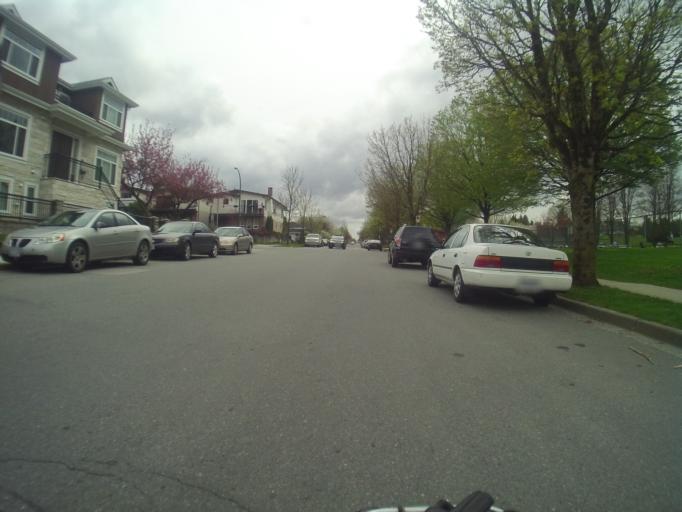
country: CA
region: British Columbia
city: Vancouver
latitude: 49.2388
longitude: -123.0741
